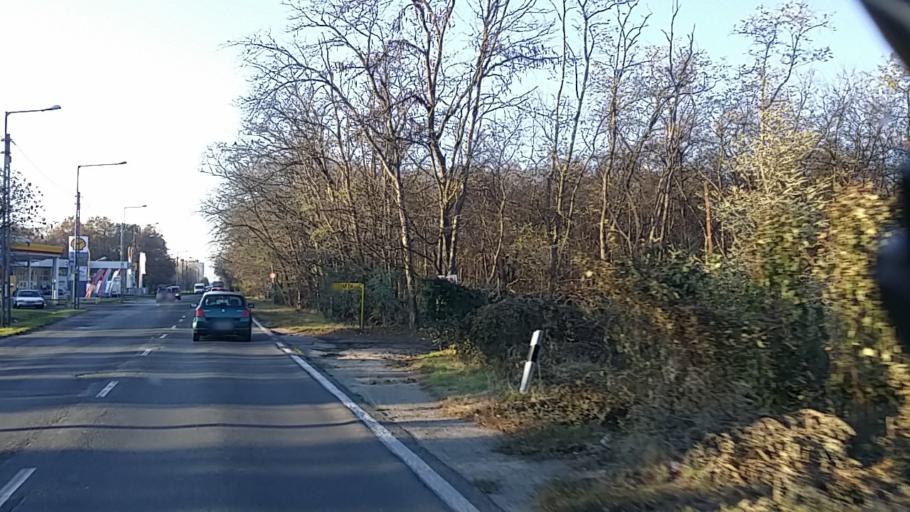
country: HU
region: Budapest
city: Budapest XVI. keruelet
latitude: 47.5421
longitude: 19.1516
